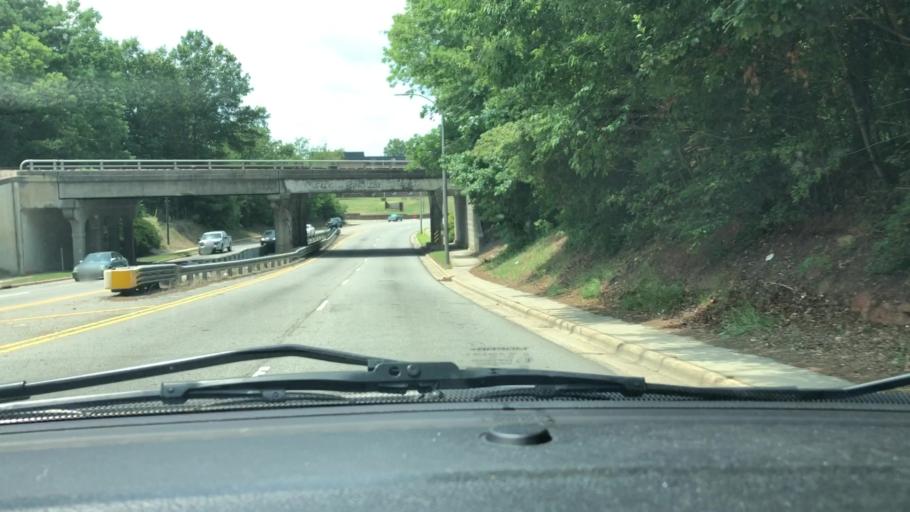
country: US
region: North Carolina
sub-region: Lee County
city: Sanford
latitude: 35.4726
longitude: -79.1758
